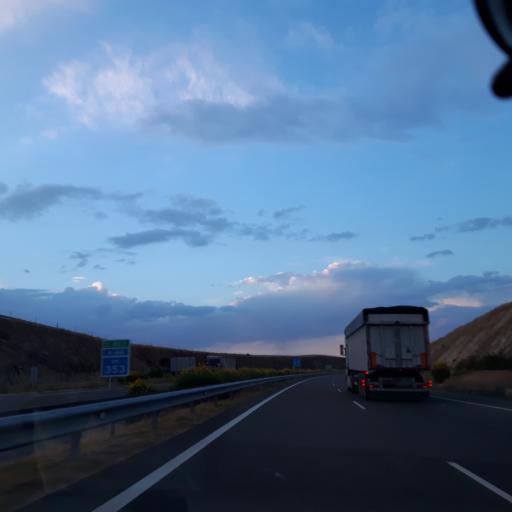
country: ES
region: Castille and Leon
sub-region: Provincia de Salamanca
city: Mozarbez
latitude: 40.8654
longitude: -5.6480
